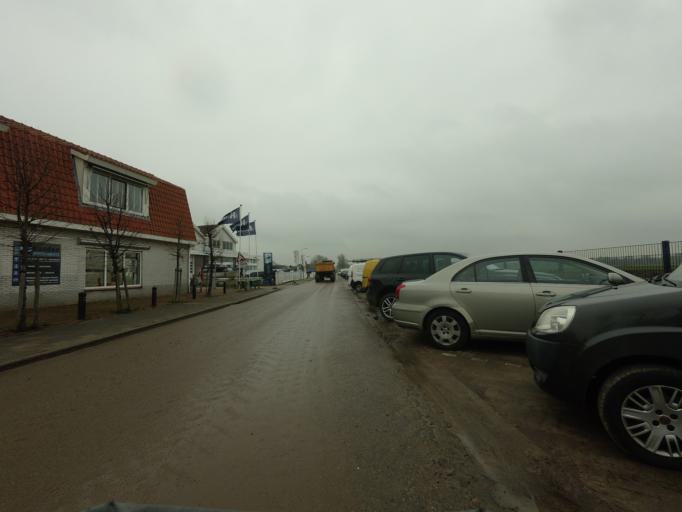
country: NL
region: Utrecht
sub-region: Stichtse Vecht
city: Breukelen
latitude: 52.1836
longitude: 5.0188
